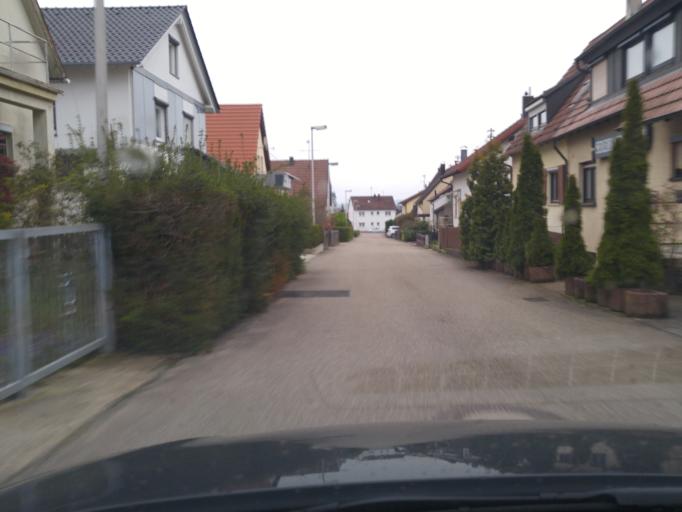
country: DE
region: Baden-Wuerttemberg
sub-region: Regierungsbezirk Stuttgart
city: Bad Wimpfen
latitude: 49.2311
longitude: 9.1507
